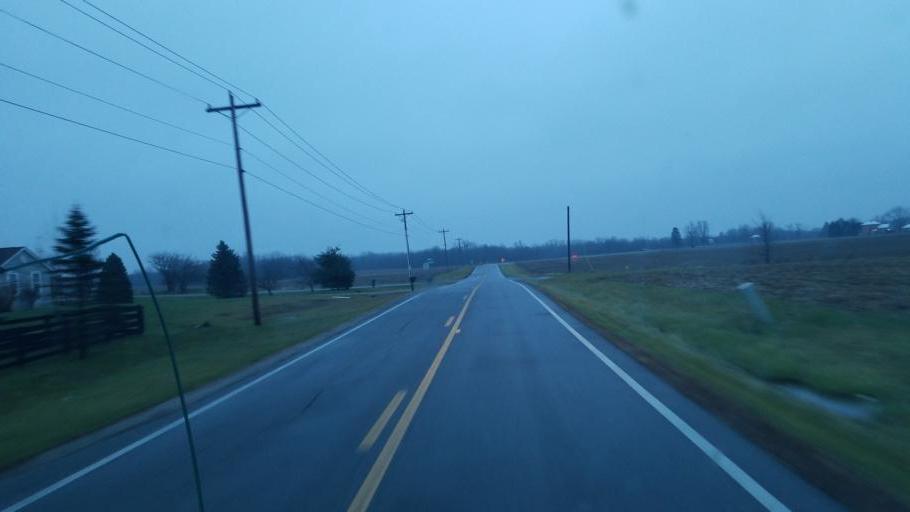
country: US
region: Ohio
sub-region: Delaware County
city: Ashley
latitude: 40.3853
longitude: -82.9456
